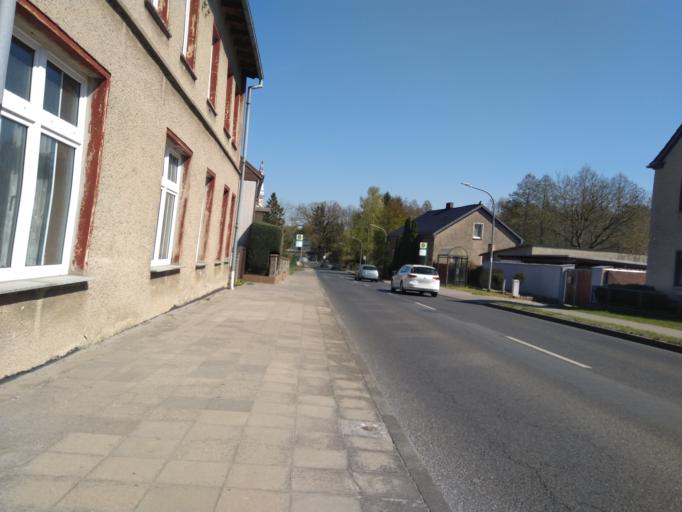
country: DE
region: Brandenburg
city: Biesenthal
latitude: 52.7665
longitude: 13.6188
